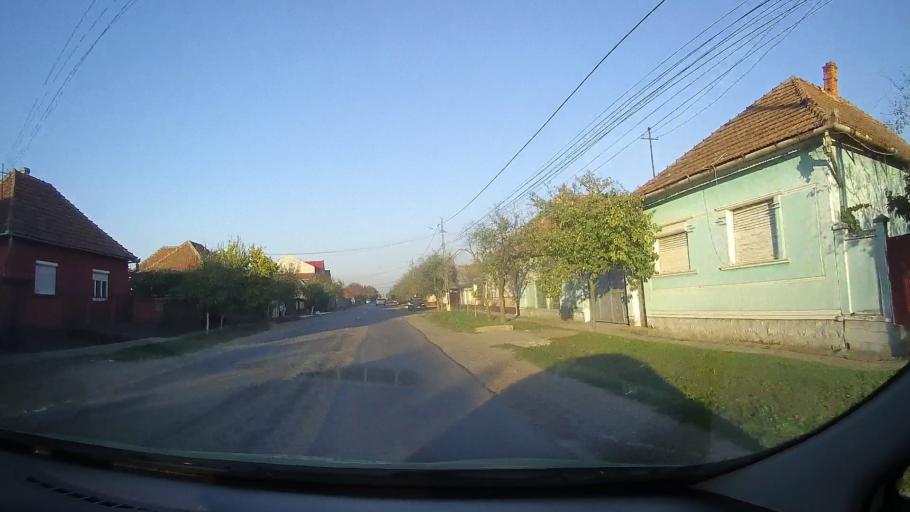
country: RO
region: Bihor
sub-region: Comuna Salard
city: Salard
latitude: 47.2145
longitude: 22.0279
